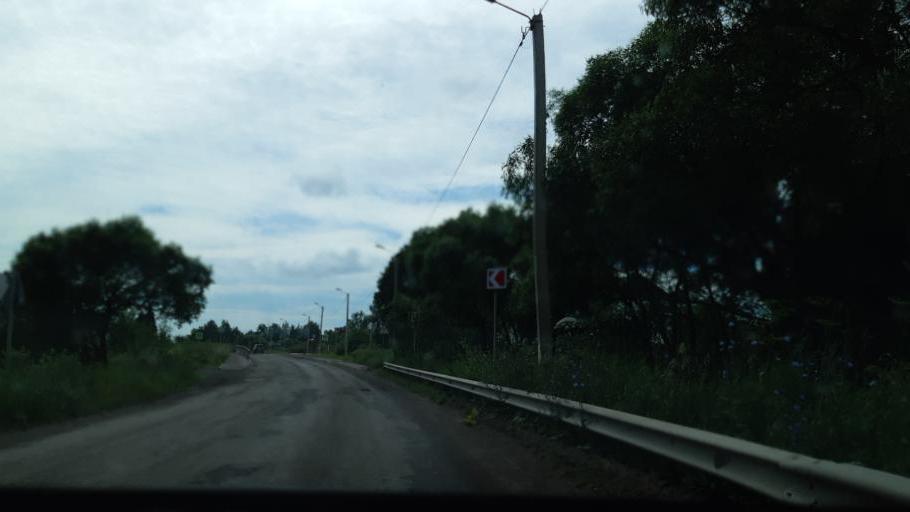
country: RU
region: Moskovskaya
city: Vereya
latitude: 55.3249
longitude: 36.1401
